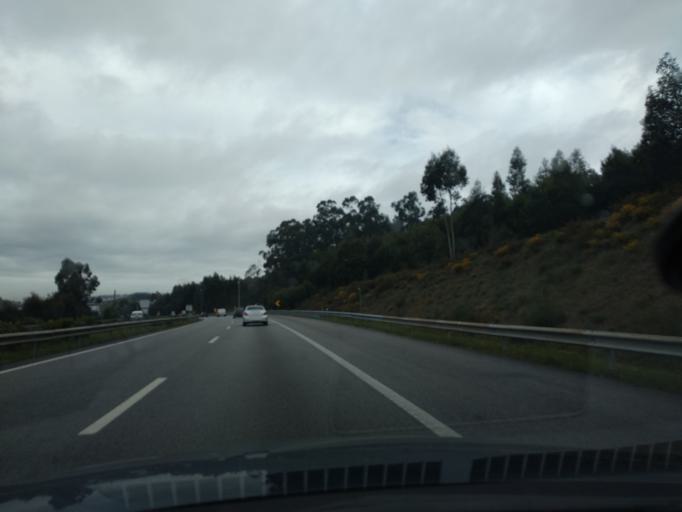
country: PT
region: Porto
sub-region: Valongo
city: Campo
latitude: 41.1949
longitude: -8.4841
